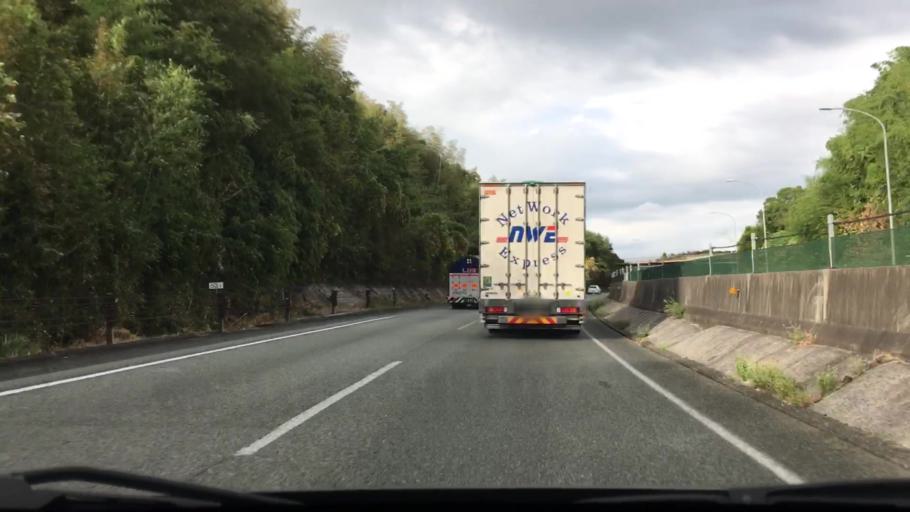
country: JP
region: Fukuoka
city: Nishifukuma
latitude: 33.7476
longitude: 130.5286
